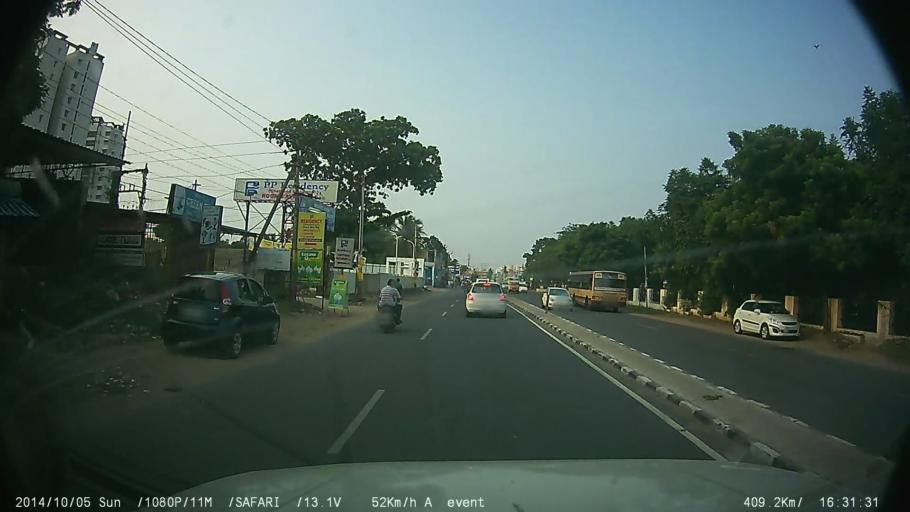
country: IN
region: Tamil Nadu
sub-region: Kancheepuram
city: Vengavasal
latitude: 12.7999
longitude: 80.2235
